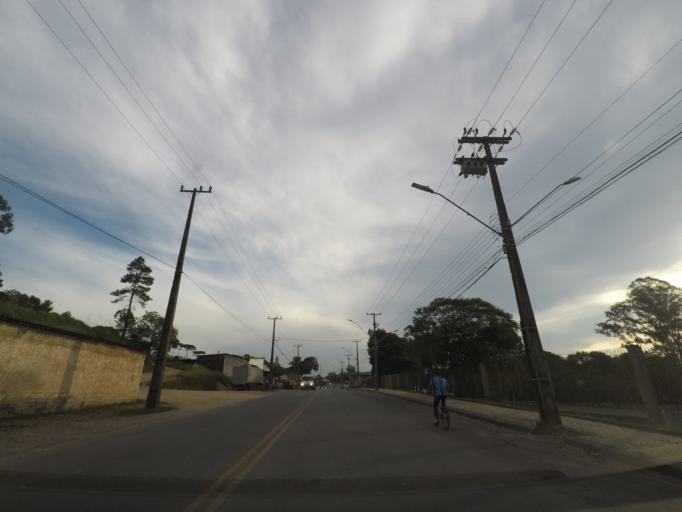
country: BR
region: Parana
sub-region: Colombo
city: Colombo
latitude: -25.2898
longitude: -49.2189
